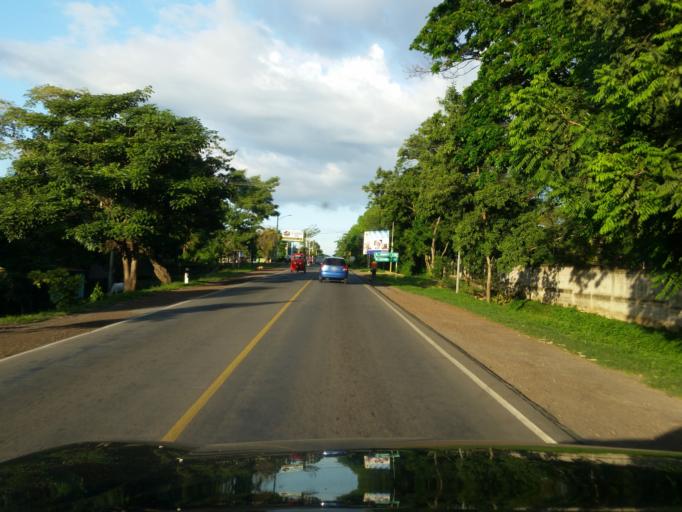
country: NI
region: Granada
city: Diriomo
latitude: 11.8498
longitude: -86.0224
